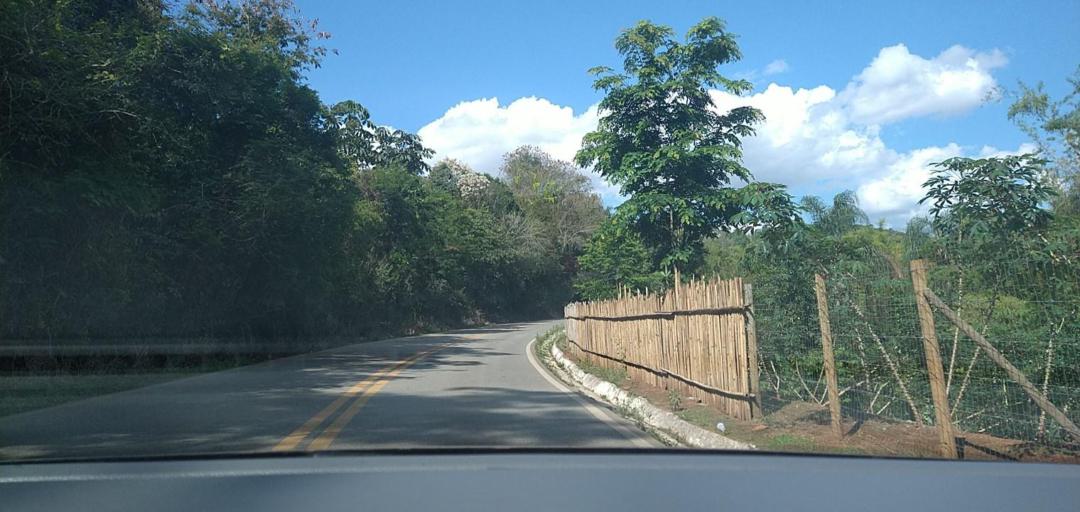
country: BR
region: Minas Gerais
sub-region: Rio Piracicaba
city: Rio Piracicaba
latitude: -19.9512
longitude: -43.1740
